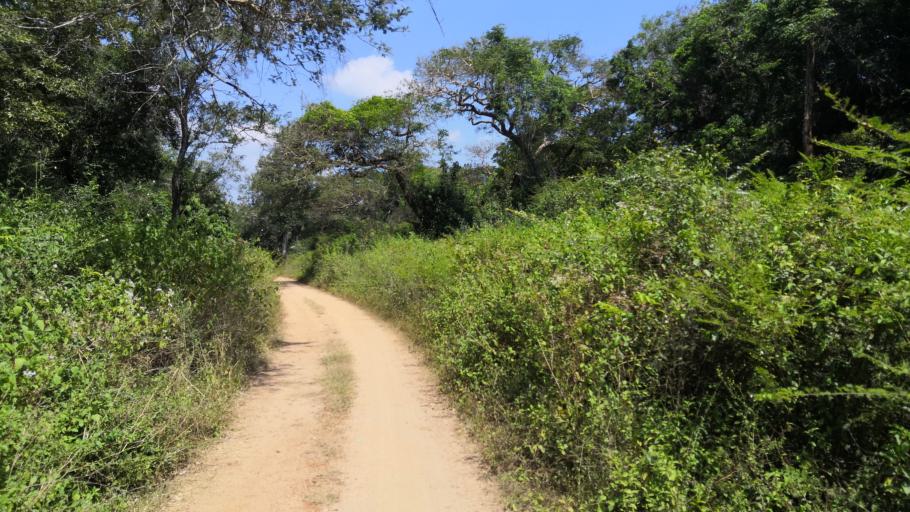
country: LK
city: Padaviya Divisional Secretariat
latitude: 8.9601
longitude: 80.6958
